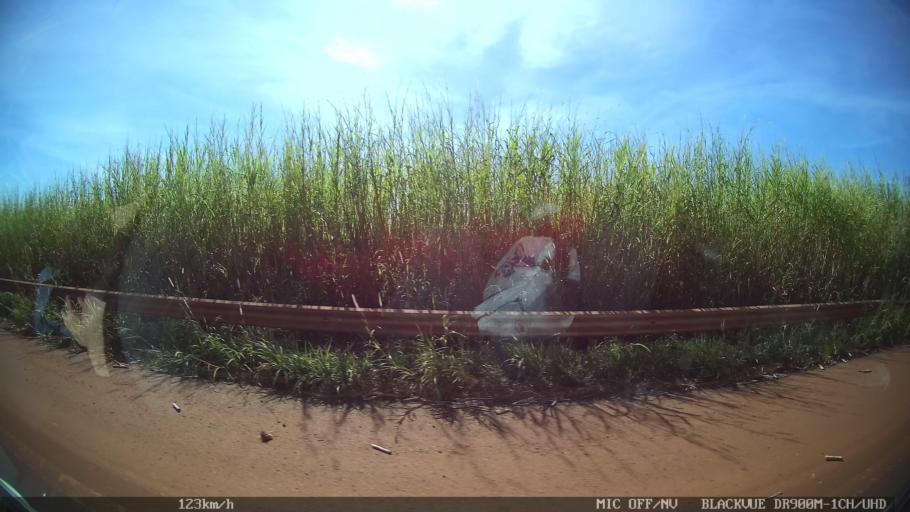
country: BR
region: Sao Paulo
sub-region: Sao Joaquim Da Barra
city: Sao Joaquim da Barra
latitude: -20.5477
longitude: -47.7631
